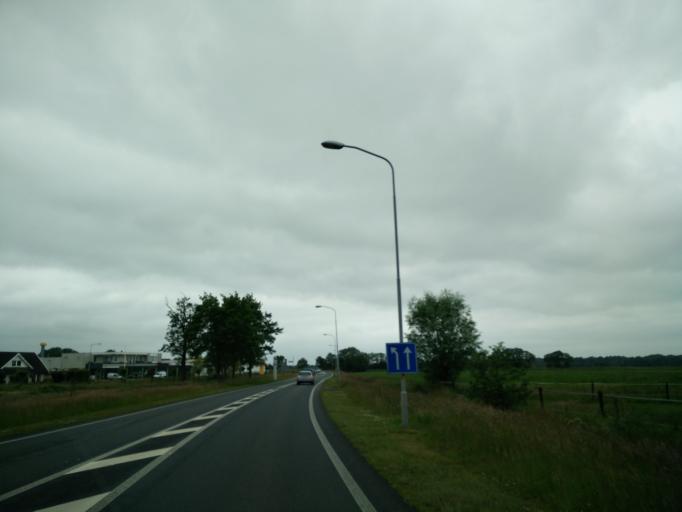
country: NL
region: Groningen
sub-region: Gemeente Groningen
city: Groningen
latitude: 53.1560
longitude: 6.4919
